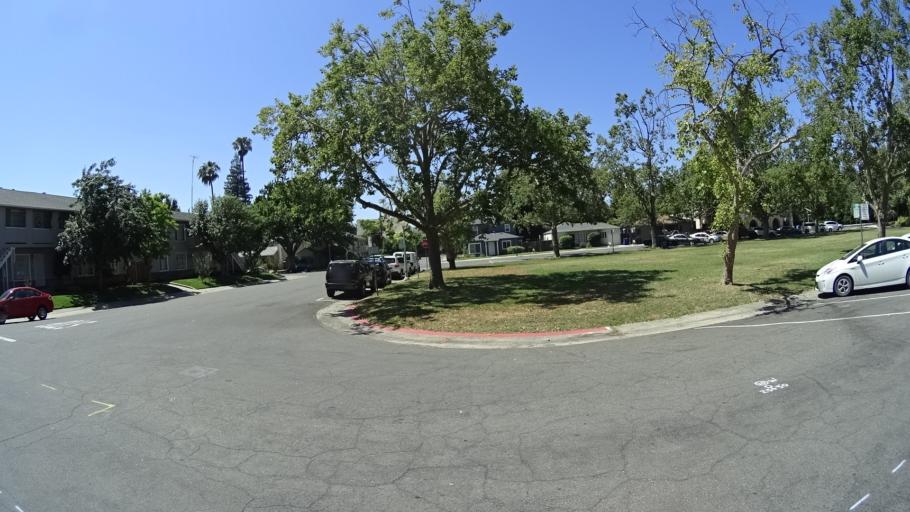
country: US
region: California
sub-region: Sacramento County
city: Sacramento
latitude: 38.5440
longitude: -121.4900
